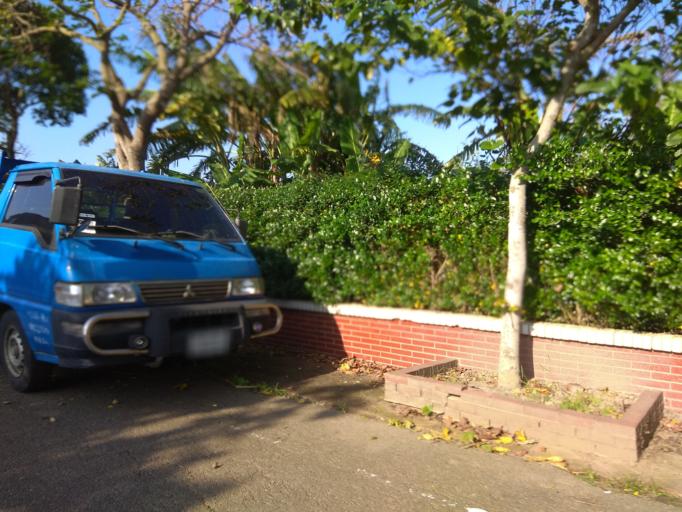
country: TW
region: Taiwan
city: Taoyuan City
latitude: 25.0502
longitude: 121.2293
